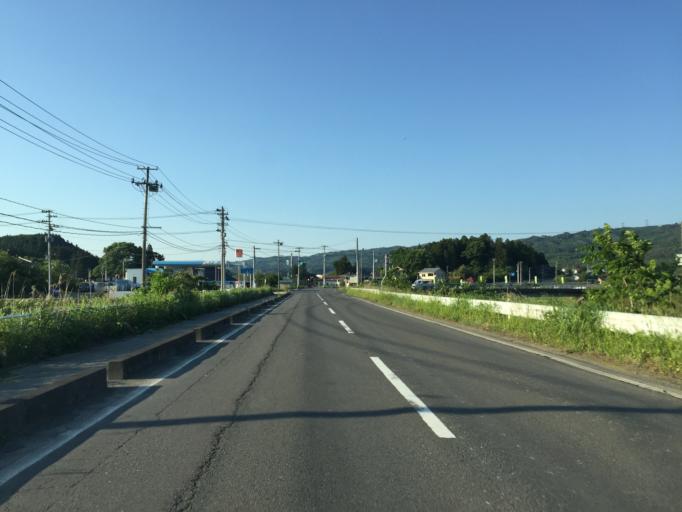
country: JP
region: Fukushima
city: Ishikawa
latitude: 36.9626
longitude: 140.4285
